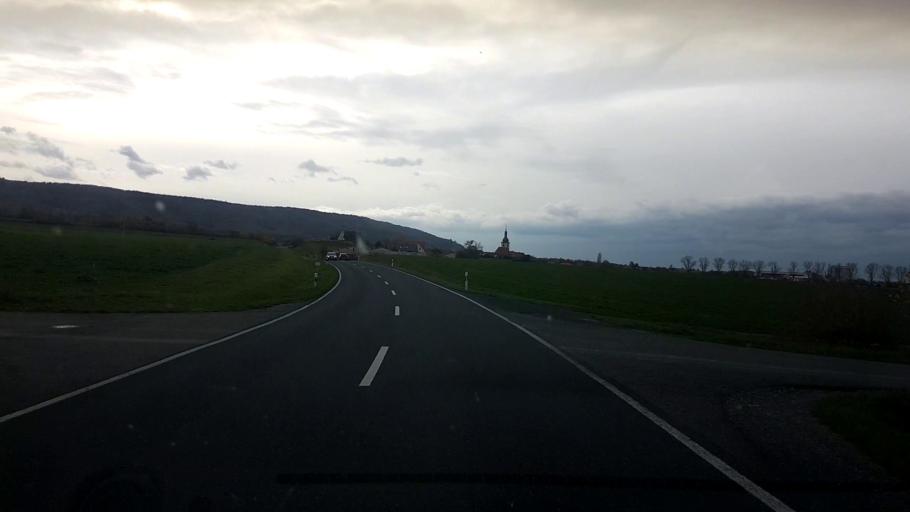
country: DE
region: Bavaria
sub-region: Regierungsbezirk Unterfranken
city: Wiesenbronn
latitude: 49.7534
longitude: 10.3125
